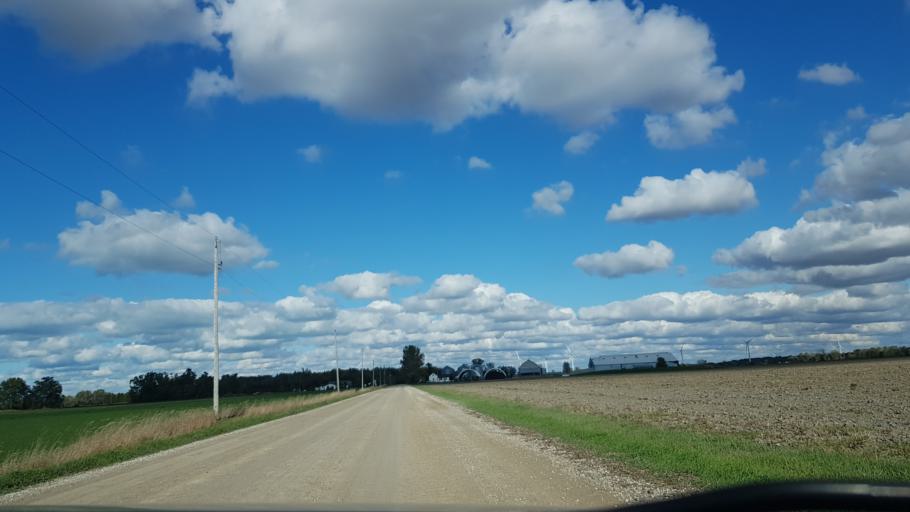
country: CA
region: Ontario
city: Lambton Shores
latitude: 43.2271
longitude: -81.7955
